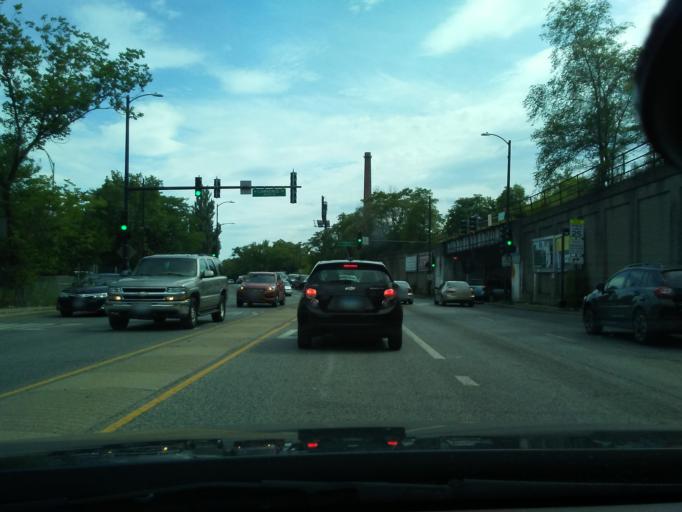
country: US
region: Illinois
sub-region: Cook County
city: Lincolnwood
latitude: 41.9686
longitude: -87.7476
